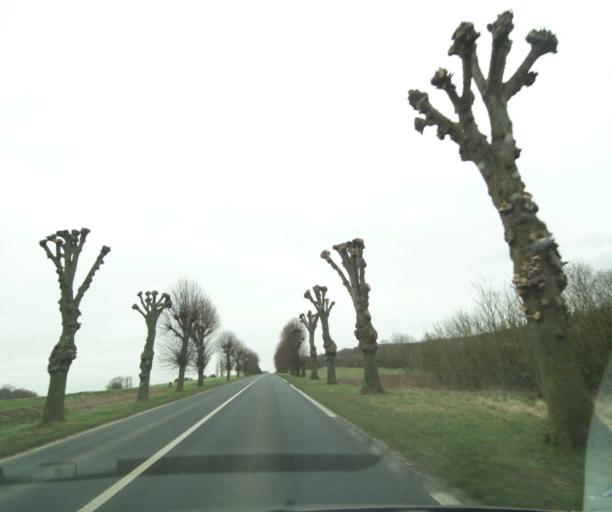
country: FR
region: Picardie
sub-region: Departement de l'Oise
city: Crisolles
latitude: 49.6057
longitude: 3.0155
